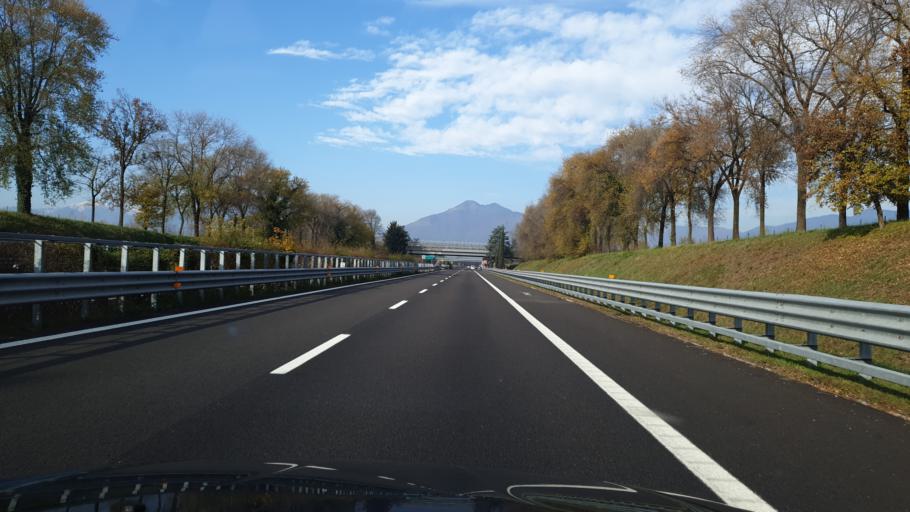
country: IT
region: Veneto
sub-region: Provincia di Vicenza
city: Thiene
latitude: 45.6779
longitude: 11.4654
